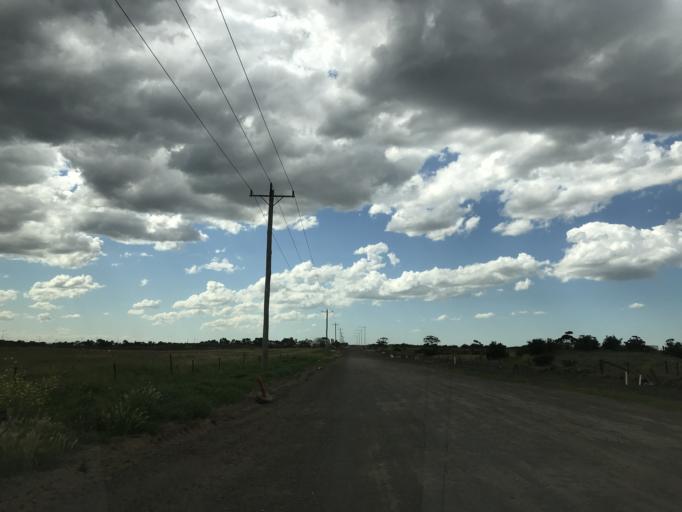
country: AU
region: Victoria
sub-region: Wyndham
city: Truganina
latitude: -37.8178
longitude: 144.7221
